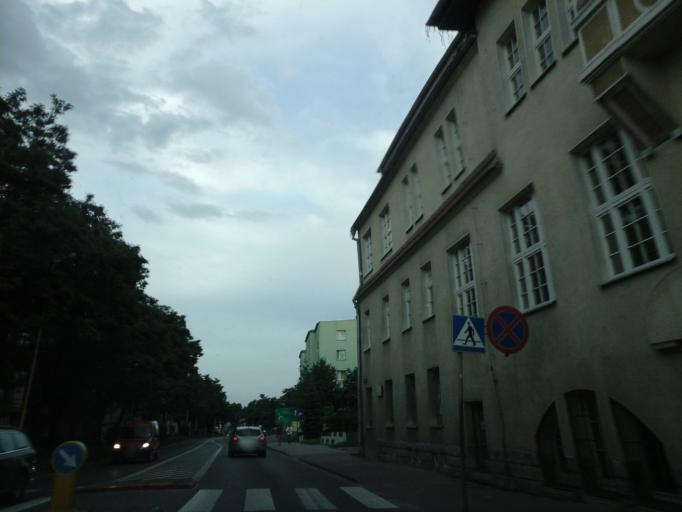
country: PL
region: West Pomeranian Voivodeship
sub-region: Powiat goleniowski
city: Nowogard
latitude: 53.6712
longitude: 15.1198
